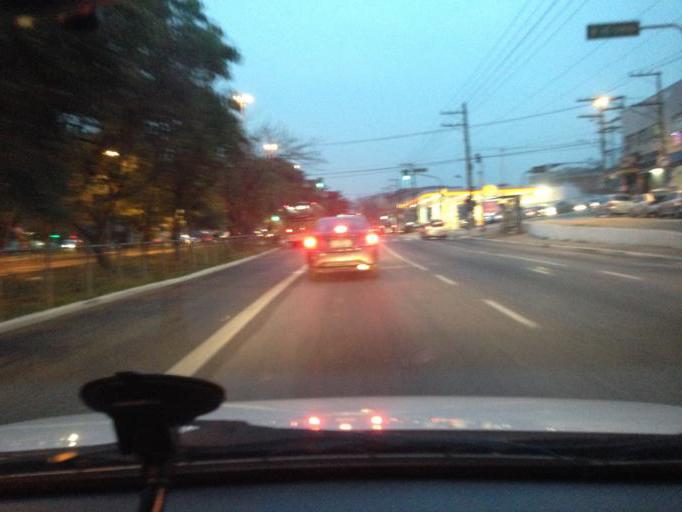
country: BR
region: Sao Paulo
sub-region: Osasco
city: Osasco
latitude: -23.4906
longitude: -46.7100
